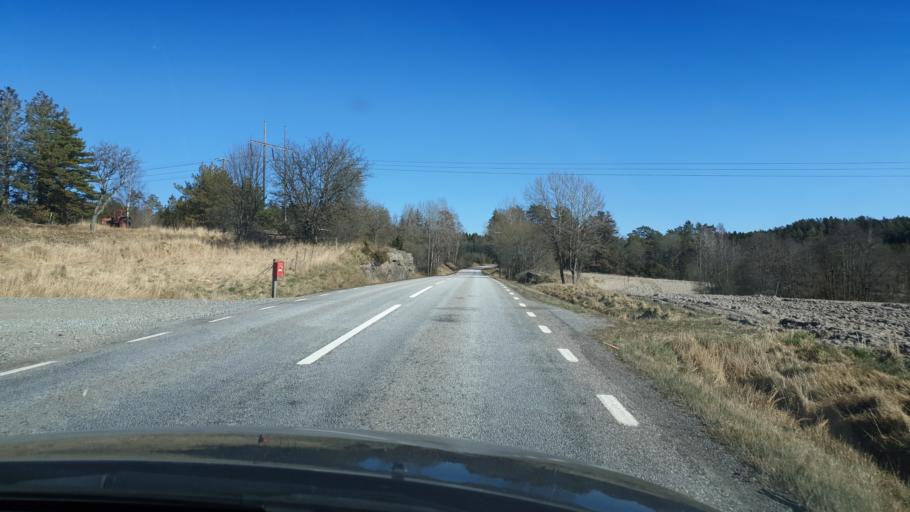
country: SE
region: Vaestra Goetaland
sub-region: Tanums Kommun
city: Tanumshede
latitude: 58.7284
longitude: 11.3922
